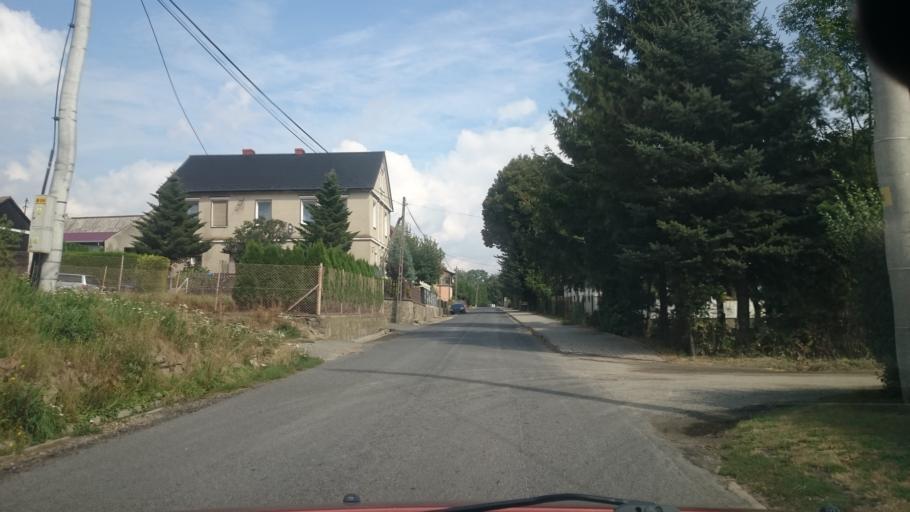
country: PL
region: Opole Voivodeship
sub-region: Powiat nyski
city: Kamiennik
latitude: 50.5415
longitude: 17.0891
